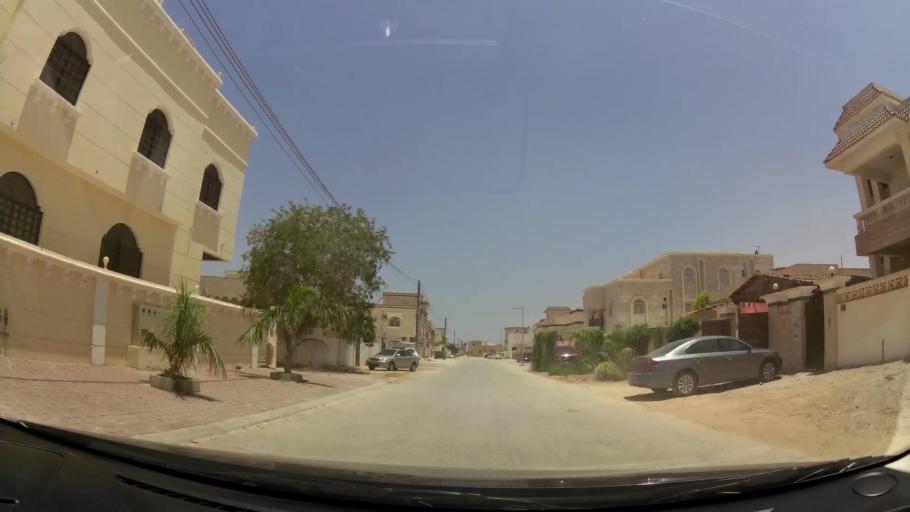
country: OM
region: Zufar
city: Salalah
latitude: 17.0715
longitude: 54.1553
